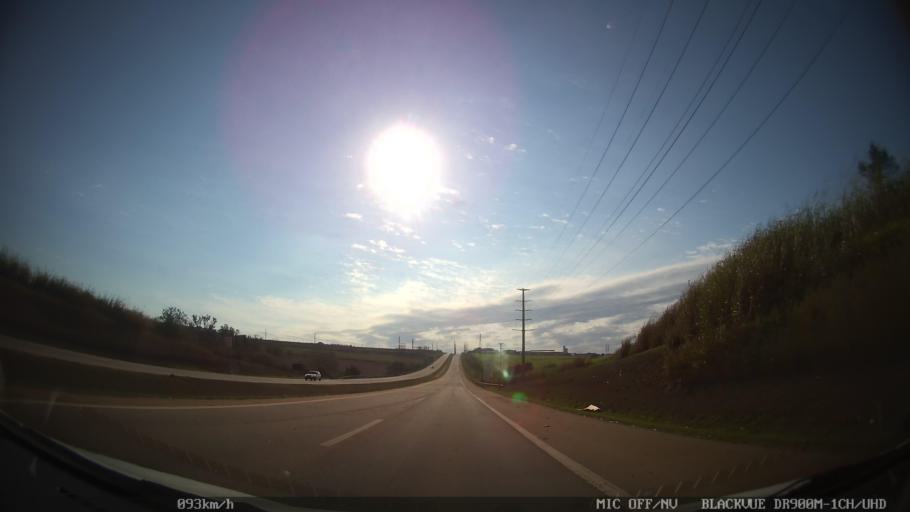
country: BR
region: Sao Paulo
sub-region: Piracicaba
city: Piracicaba
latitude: -22.6765
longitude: -47.5979
